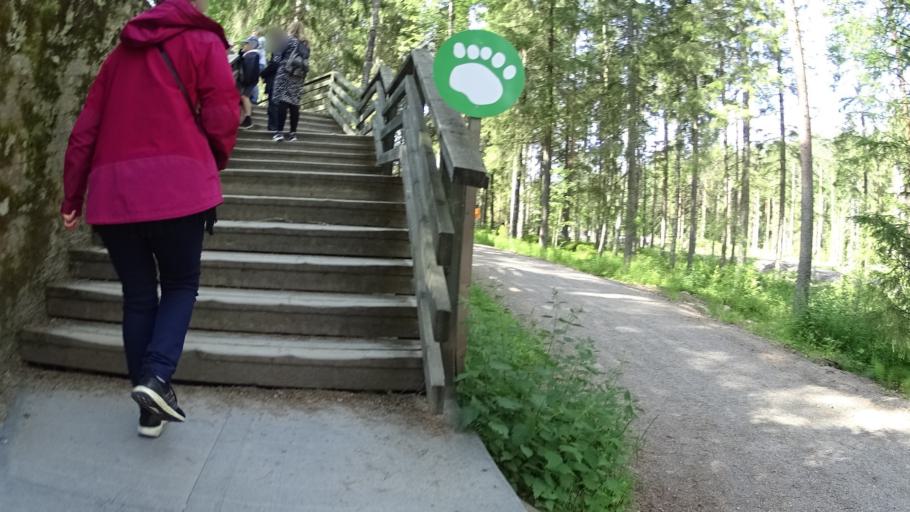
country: FI
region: Southern Ostrobothnia
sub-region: Kuusiokunnat
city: AEhtaeri
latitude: 62.5392
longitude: 24.1845
